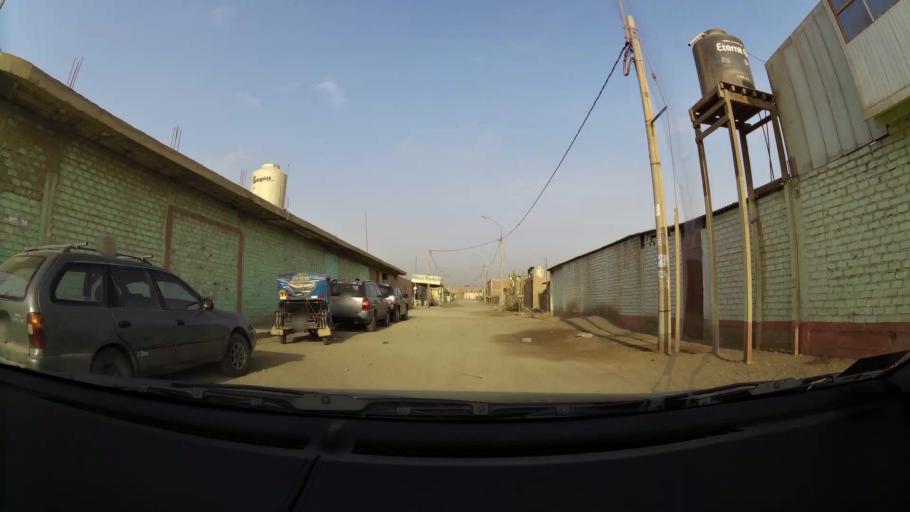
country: PE
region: Lima
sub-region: Lima
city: Santa Rosa
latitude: -11.7479
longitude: -77.1514
